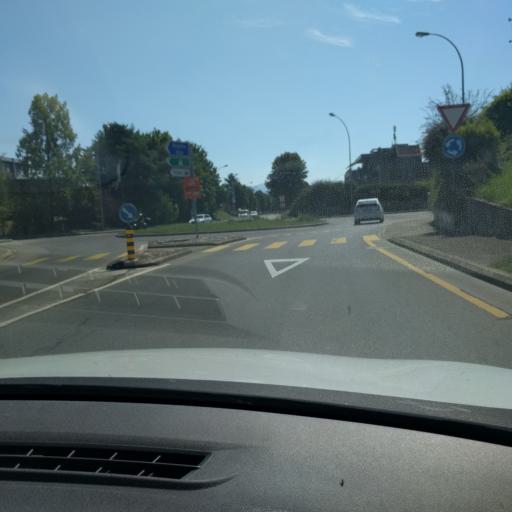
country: CH
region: Vaud
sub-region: Nyon District
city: Gland
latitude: 46.4172
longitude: 6.2699
